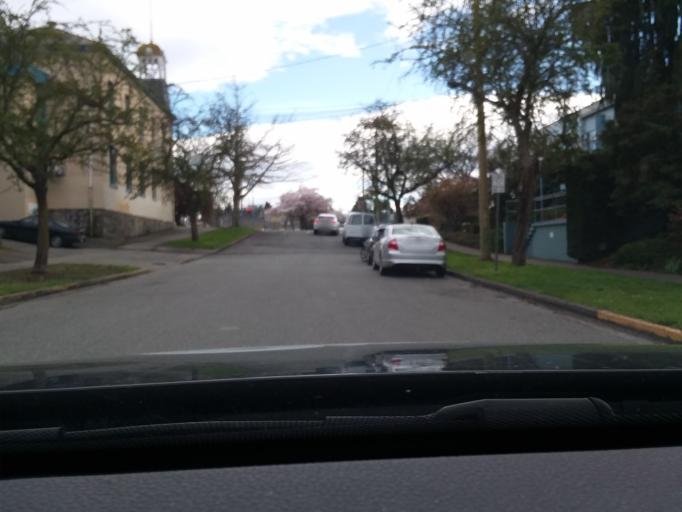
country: CA
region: British Columbia
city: Victoria
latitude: 48.4252
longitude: -123.3474
